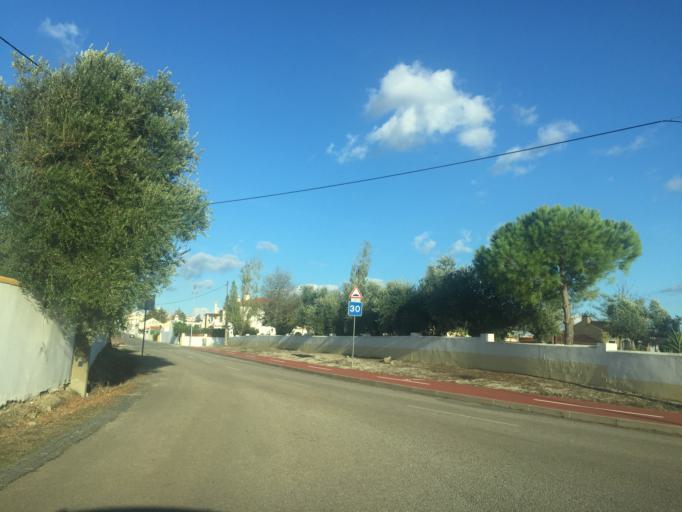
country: PT
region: Portalegre
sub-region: Alter do Chao
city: Alter do Chao
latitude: 39.1971
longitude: -7.6672
